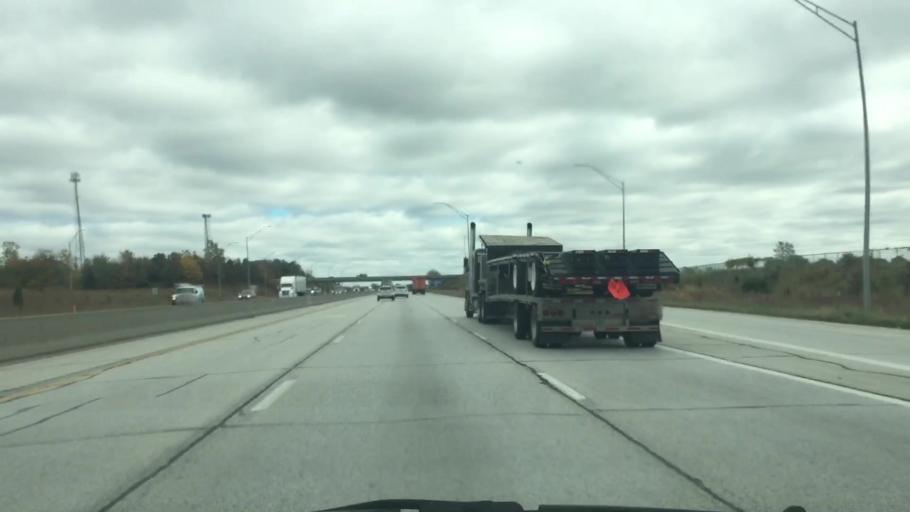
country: US
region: Iowa
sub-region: Polk County
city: Altoona
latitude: 41.6591
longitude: -93.5275
